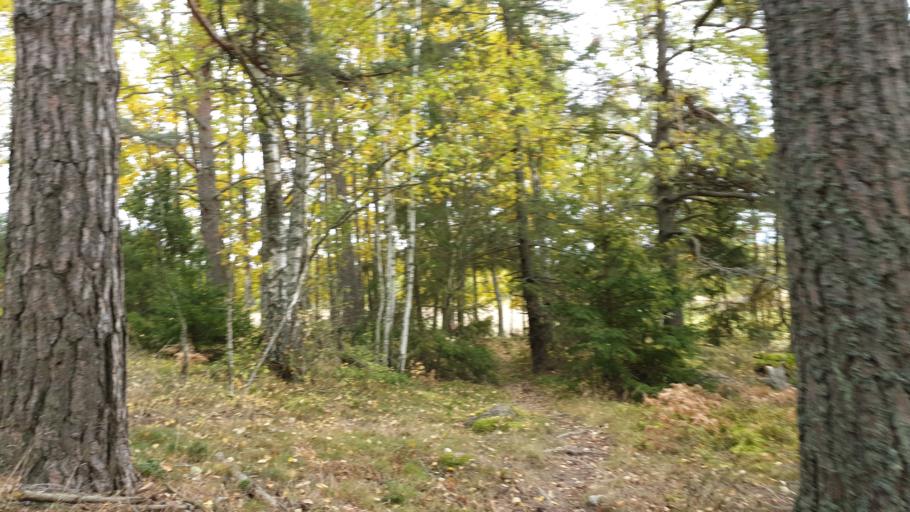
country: SE
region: Vaestmanland
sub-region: Sala Kommun
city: Sala
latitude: 59.8150
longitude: 16.6516
